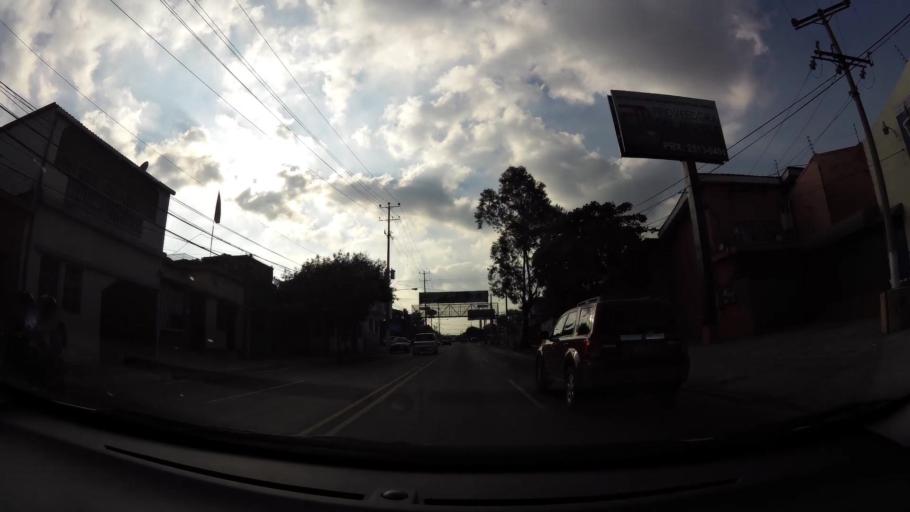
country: SV
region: San Salvador
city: San Salvador
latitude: 13.6917
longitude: -89.2127
